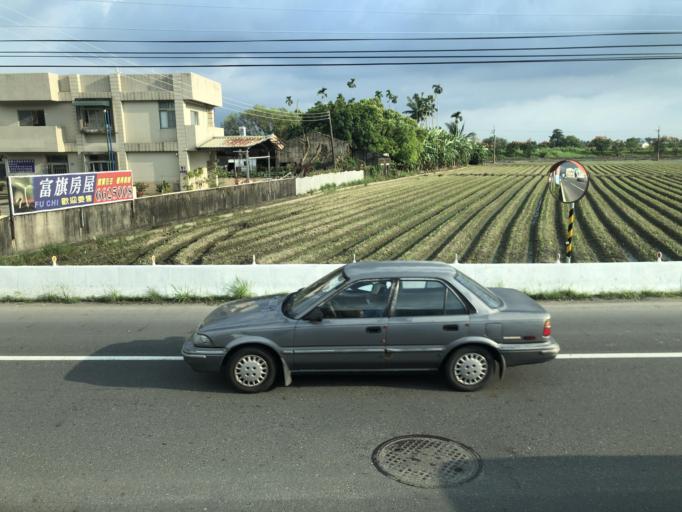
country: TW
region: Taiwan
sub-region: Pingtung
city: Pingtung
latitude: 22.9010
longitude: 120.5275
